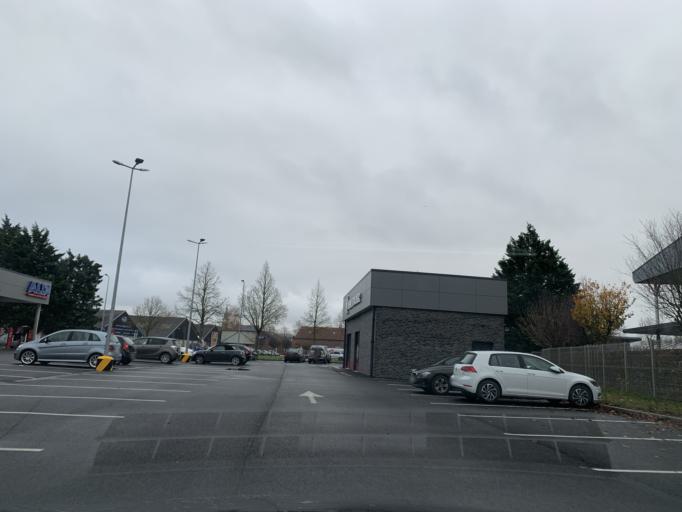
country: FR
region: Nord-Pas-de-Calais
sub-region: Departement du Nord
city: Neuville-Saint-Remy
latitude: 50.1767
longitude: 3.2160
